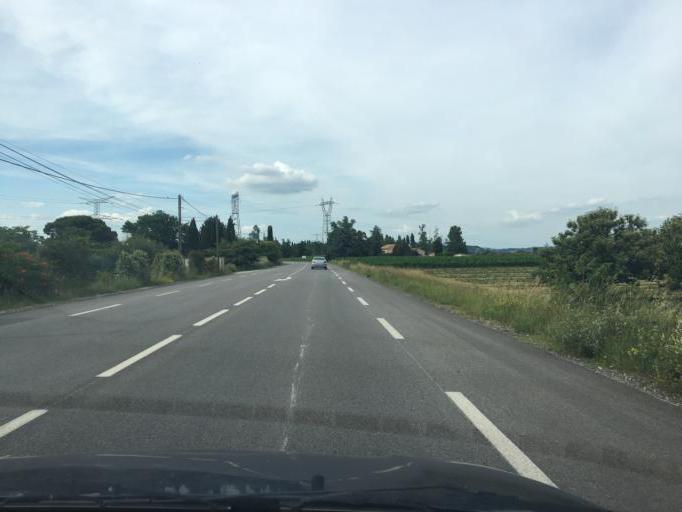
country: FR
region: Rhone-Alpes
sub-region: Departement de la Drome
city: Chateauneuf-sur-Isere
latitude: 45.0233
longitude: 4.9337
